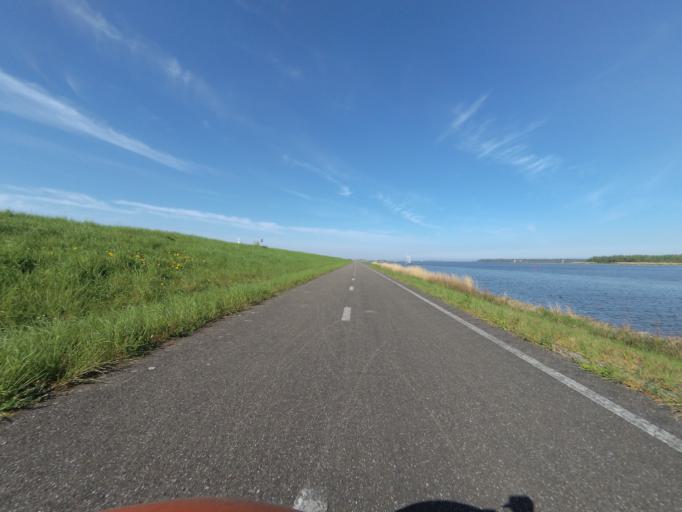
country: NL
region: Flevoland
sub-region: Gemeente Noordoostpolder
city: Ens
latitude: 52.5797
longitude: 5.7884
